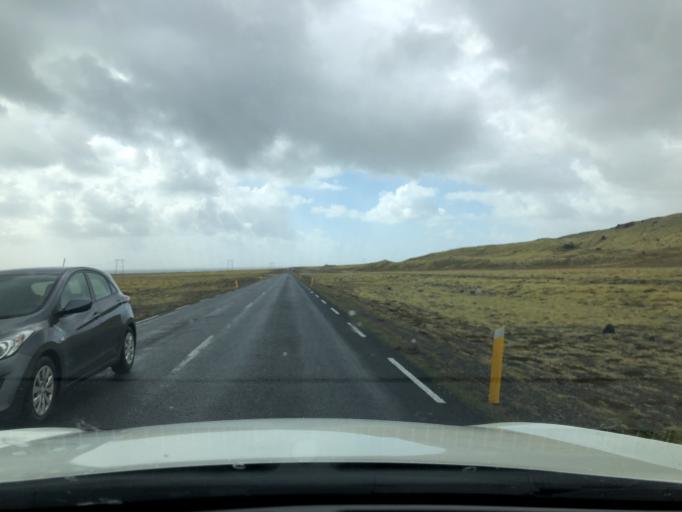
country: IS
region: East
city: Hoefn
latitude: 63.9486
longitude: -16.4269
